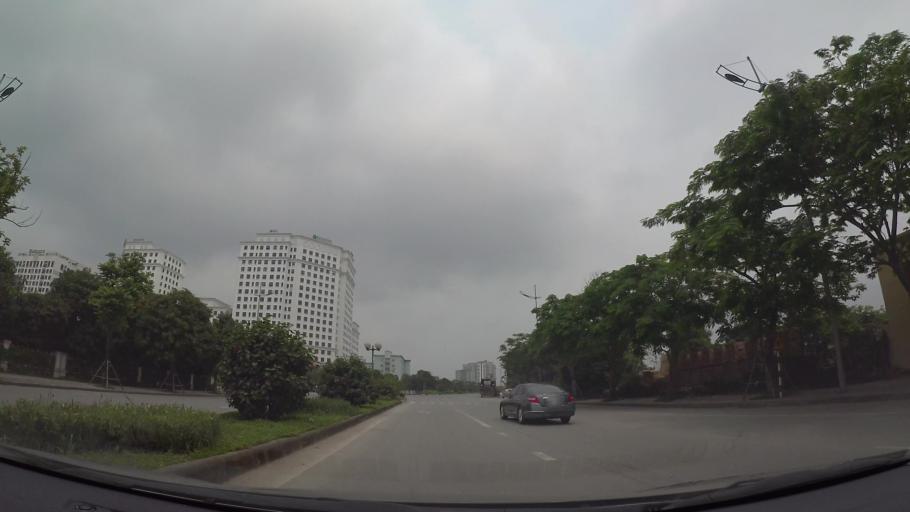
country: VN
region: Ha Noi
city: Trau Quy
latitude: 21.0555
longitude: 105.9150
